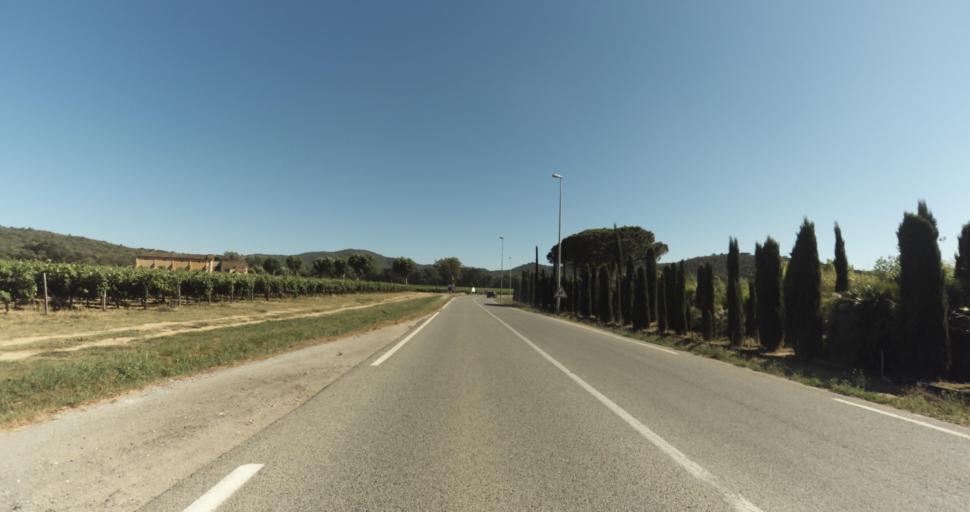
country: FR
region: Provence-Alpes-Cote d'Azur
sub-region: Departement du Var
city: Gassin
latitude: 43.2566
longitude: 6.5946
